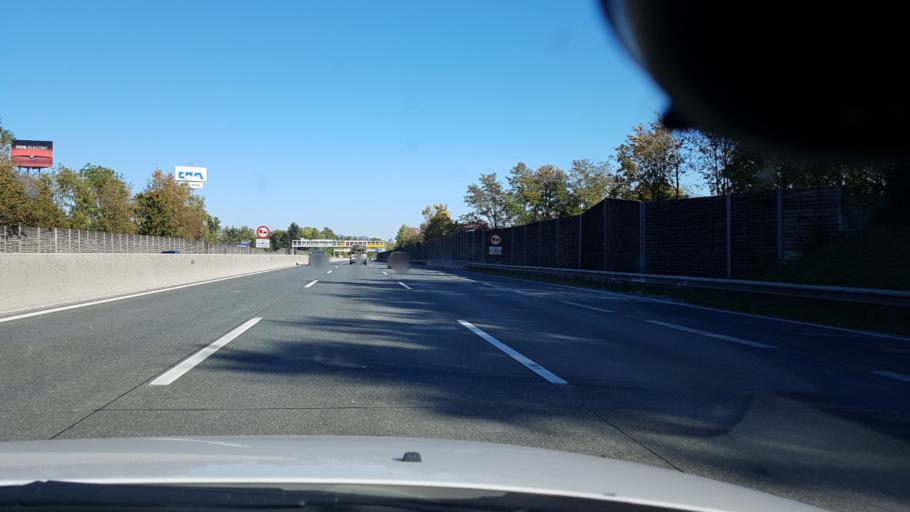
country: DE
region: Bavaria
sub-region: Upper Bavaria
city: Ainring
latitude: 47.7861
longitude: 12.9815
